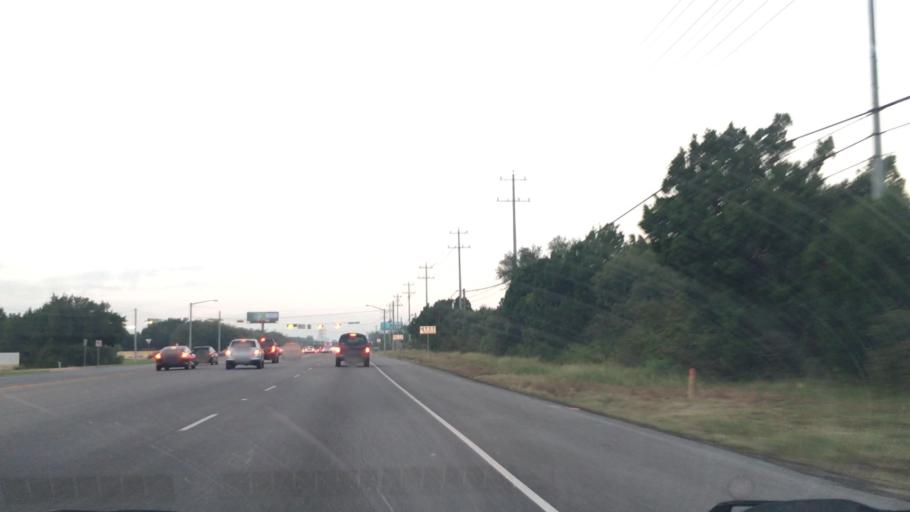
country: US
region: Texas
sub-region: Williamson County
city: Anderson Mill
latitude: 30.4080
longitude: -97.8519
